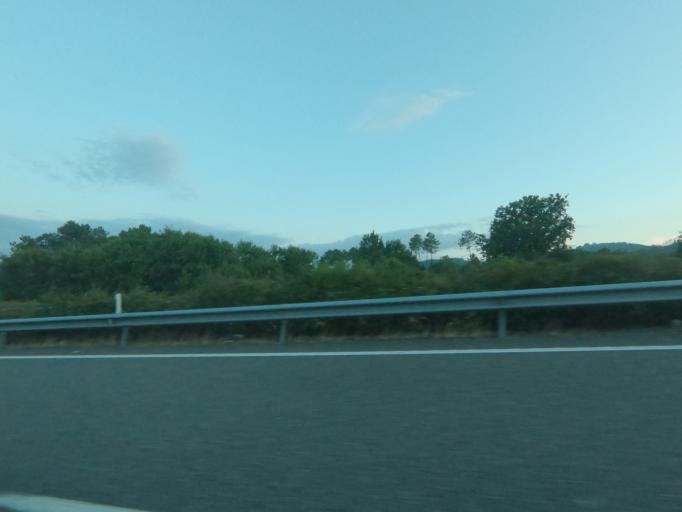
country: ES
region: Galicia
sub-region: Provincia de Pontevedra
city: Ponteareas
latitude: 42.1622
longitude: -8.5309
